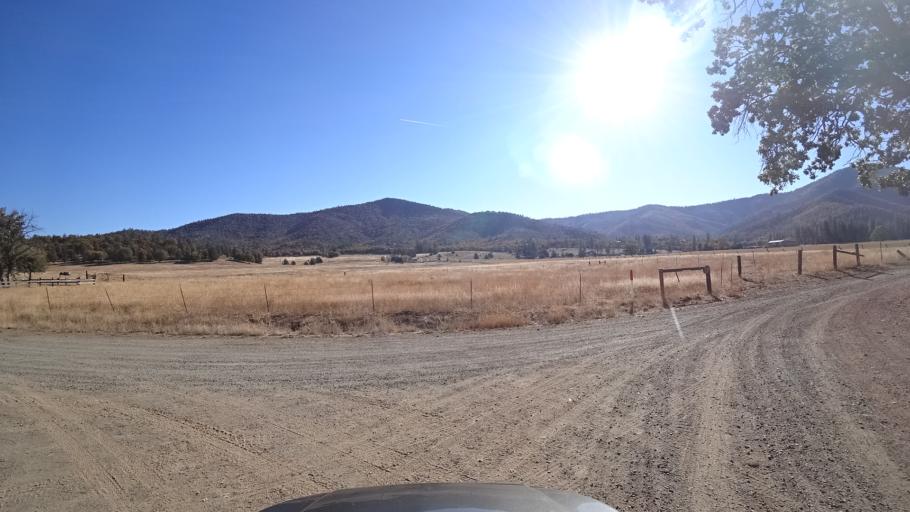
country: US
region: California
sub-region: Siskiyou County
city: Yreka
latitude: 41.5716
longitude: -122.7926
